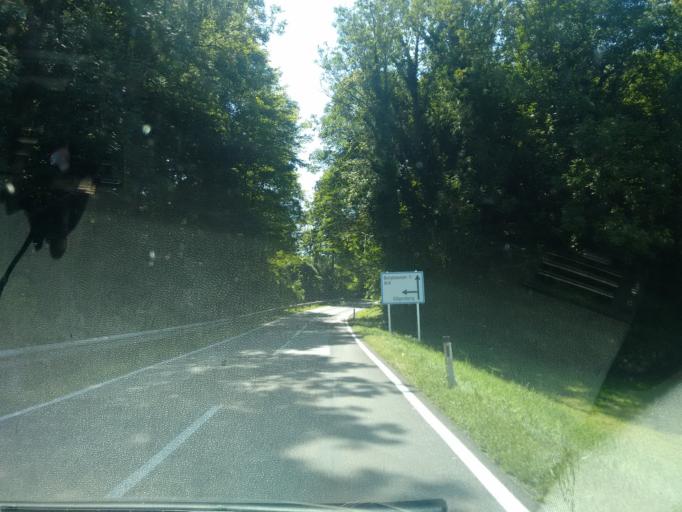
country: DE
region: Bavaria
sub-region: Lower Bavaria
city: Julbach
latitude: 48.2092
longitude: 12.9690
